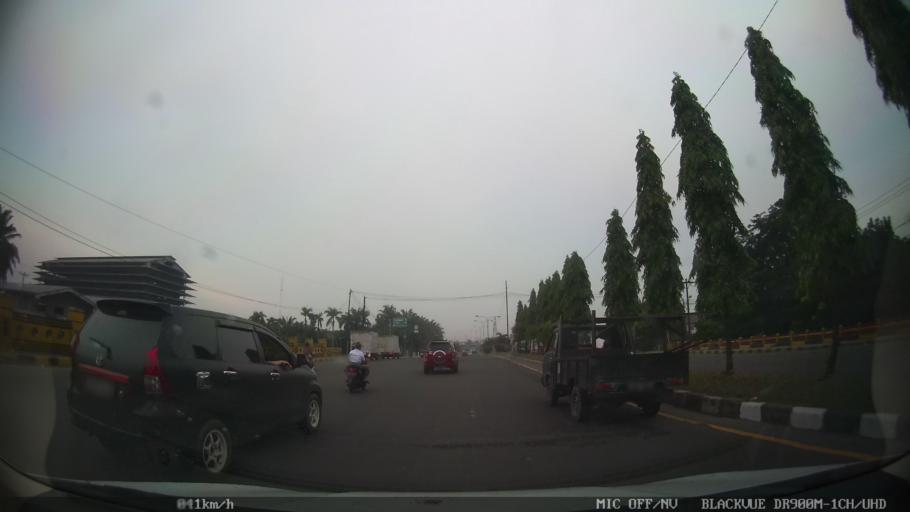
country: ID
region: North Sumatra
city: Deli Tua
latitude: 3.5369
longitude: 98.7135
